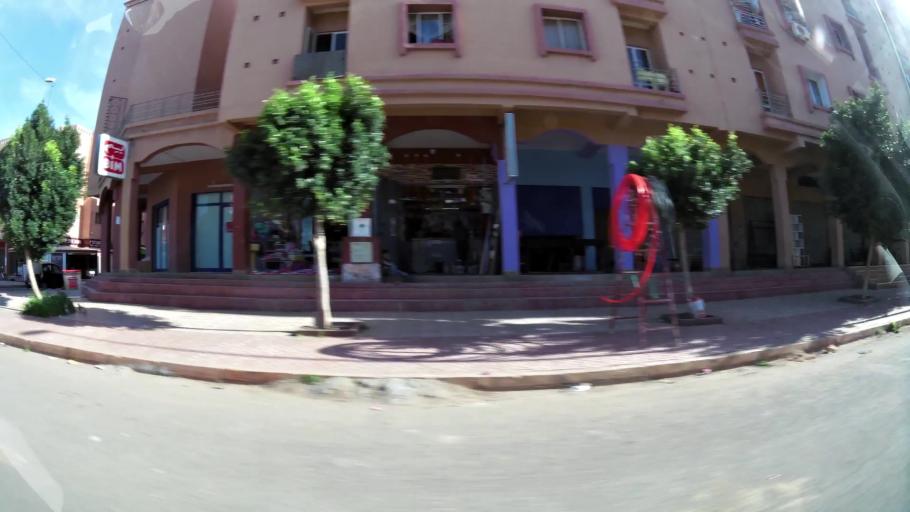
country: MA
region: Marrakech-Tensift-Al Haouz
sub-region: Marrakech
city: Marrakesh
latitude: 31.6861
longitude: -8.0672
